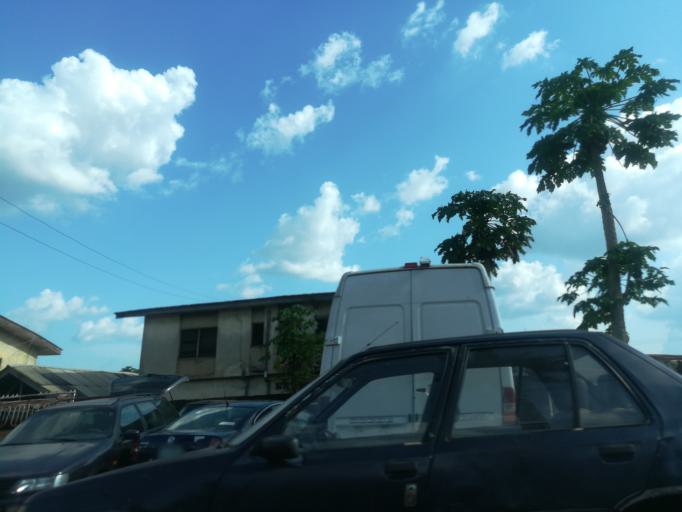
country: NG
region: Oyo
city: Ibadan
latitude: 7.4210
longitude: 3.9708
